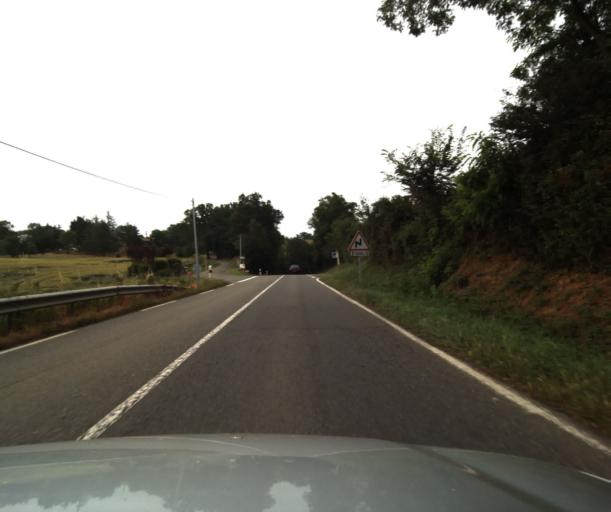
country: FR
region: Midi-Pyrenees
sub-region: Departement du Gers
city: Mielan
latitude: 43.4800
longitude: 0.3363
